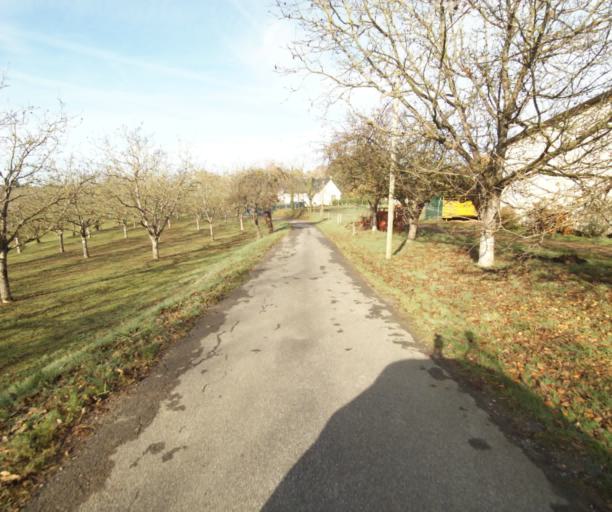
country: FR
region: Limousin
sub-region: Departement de la Correze
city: Sainte-Fortunade
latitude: 45.2249
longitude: 1.7385
